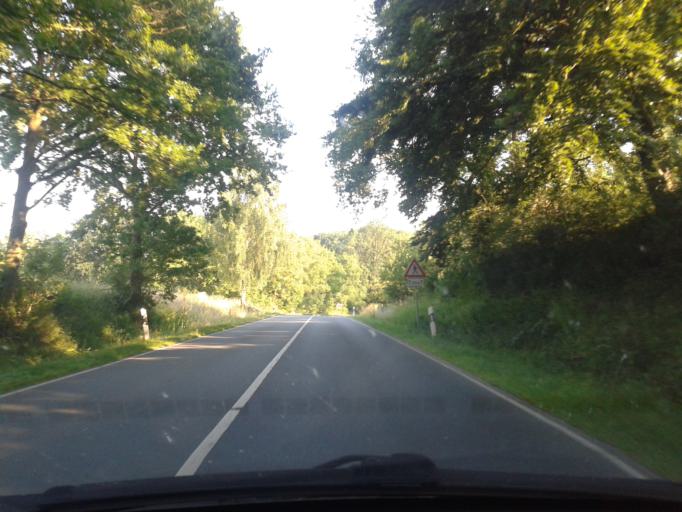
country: DE
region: North Rhine-Westphalia
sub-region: Regierungsbezirk Detmold
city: Lemgo
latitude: 52.0034
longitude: 8.9157
